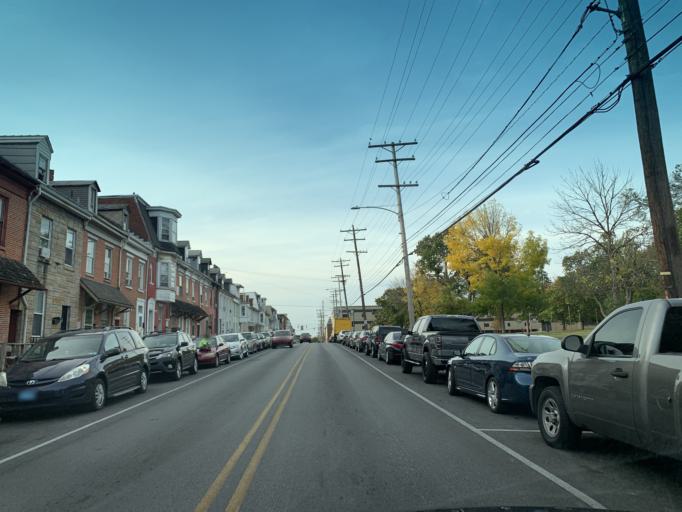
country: US
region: Pennsylvania
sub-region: York County
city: York
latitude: 39.9557
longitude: -76.7287
